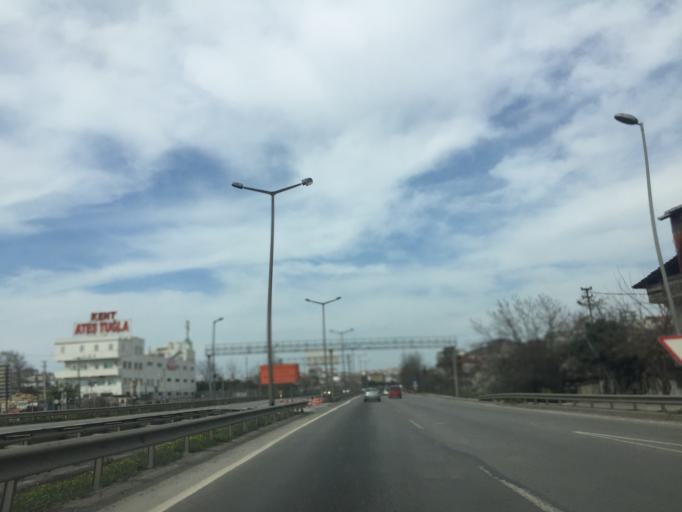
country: TR
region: Kocaeli
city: Darica
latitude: 40.8193
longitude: 29.3650
